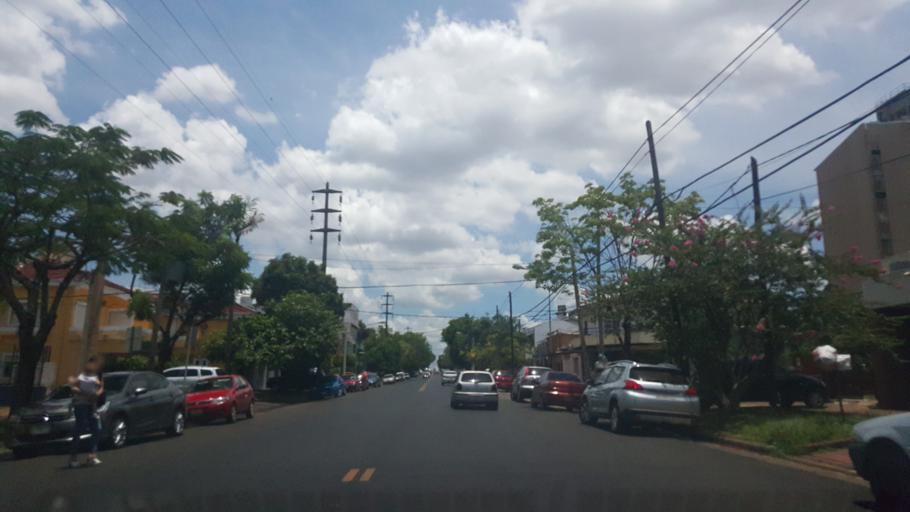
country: AR
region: Misiones
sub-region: Departamento de Capital
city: Posadas
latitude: -27.3683
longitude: -55.9053
